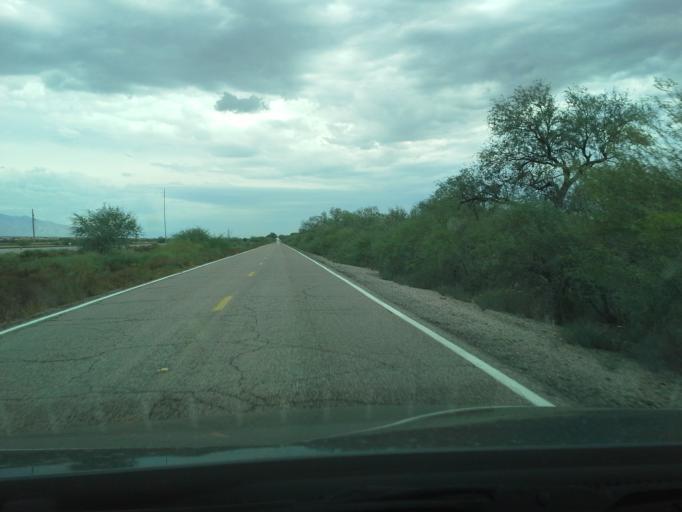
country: US
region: Arizona
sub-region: Pima County
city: Marana
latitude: 32.4725
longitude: -111.2300
